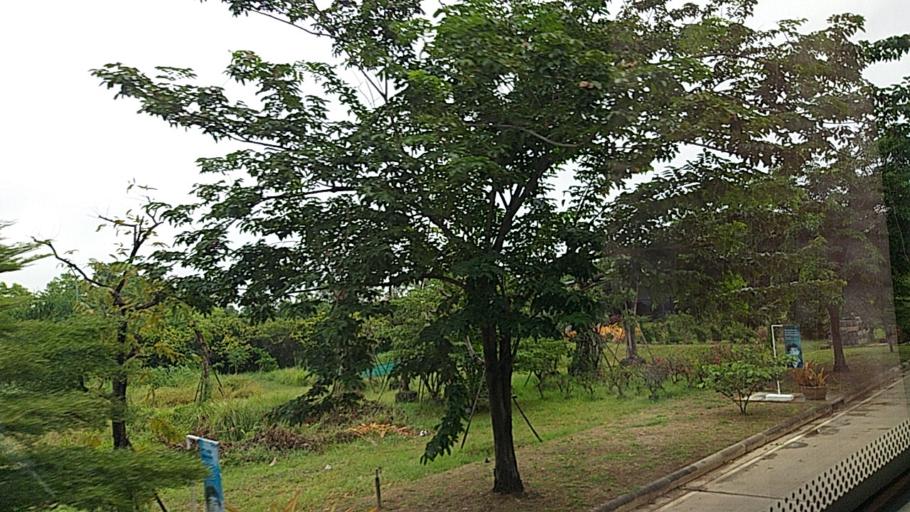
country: TH
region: Nakhon Ratchasima
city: Nakhon Ratchasima
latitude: 14.9941
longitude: 102.0922
